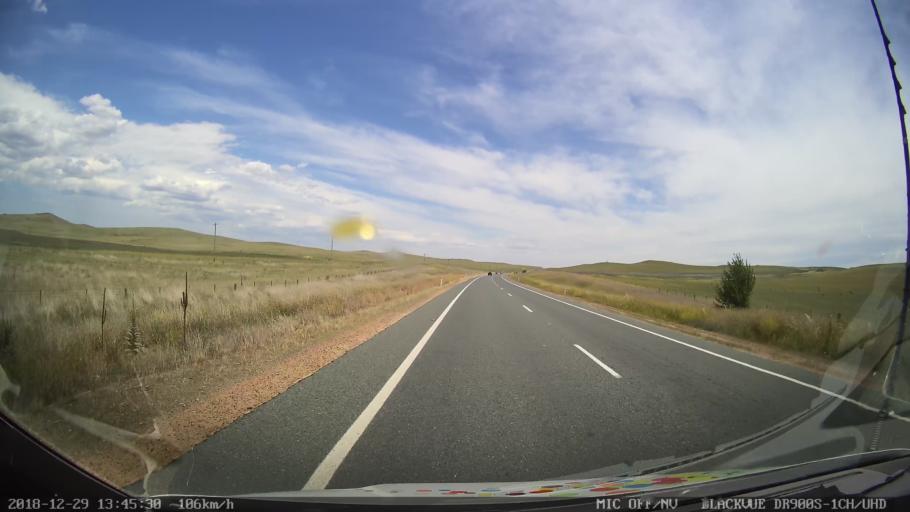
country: AU
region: New South Wales
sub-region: Cooma-Monaro
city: Cooma
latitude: -36.0976
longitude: 149.1454
